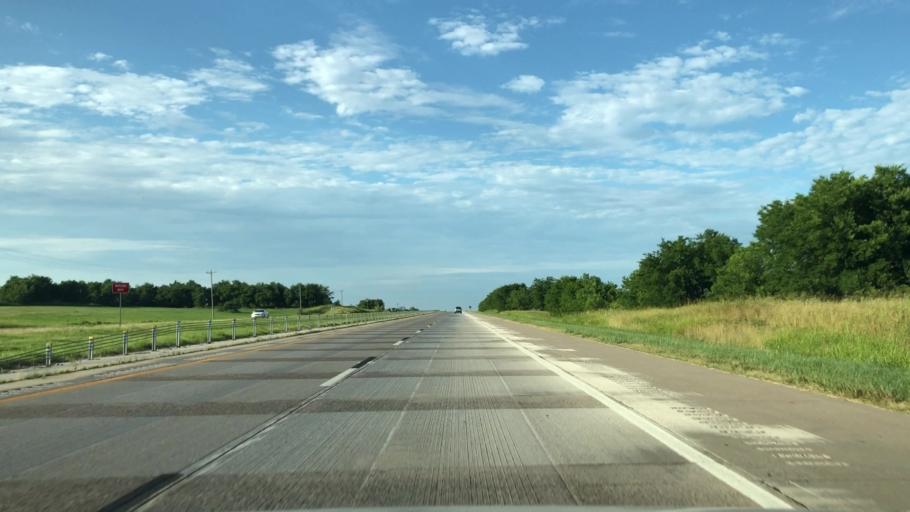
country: US
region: Oklahoma
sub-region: Osage County
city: Skiatook
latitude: 36.4307
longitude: -95.9206
